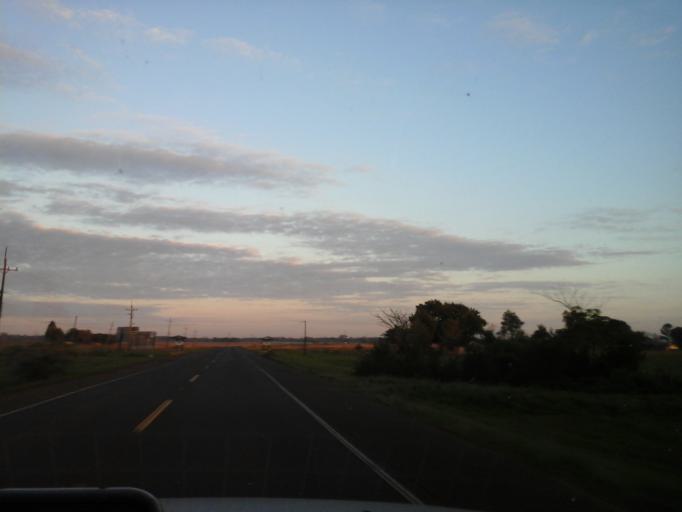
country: PY
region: Itapua
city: General Delgado
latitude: -27.0839
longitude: -56.5533
